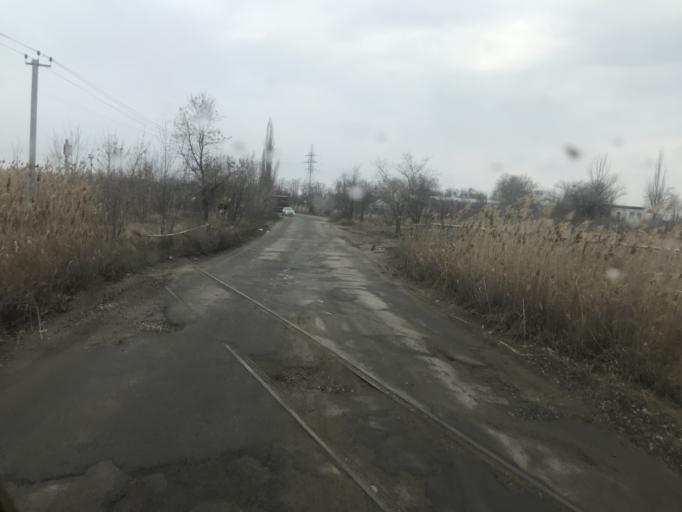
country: RU
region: Volgograd
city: Krasnoslobodsk
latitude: 48.5305
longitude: 44.5945
